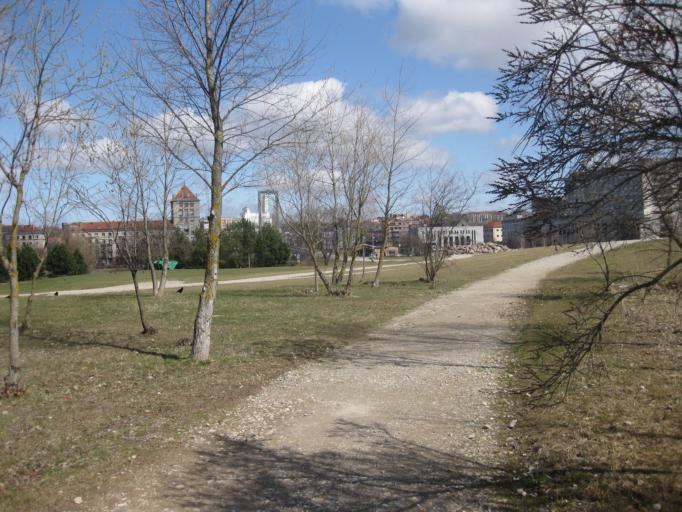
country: LT
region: Kauno apskritis
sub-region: Kaunas
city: Kaunas
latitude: 54.8923
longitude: 23.9091
